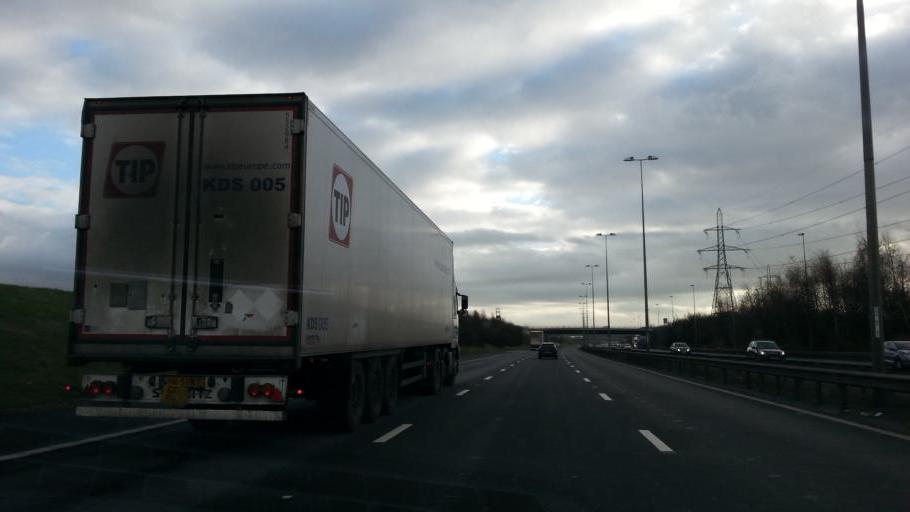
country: GB
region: England
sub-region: Solihull
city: Chelmsley Wood
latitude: 52.4973
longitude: -1.7178
